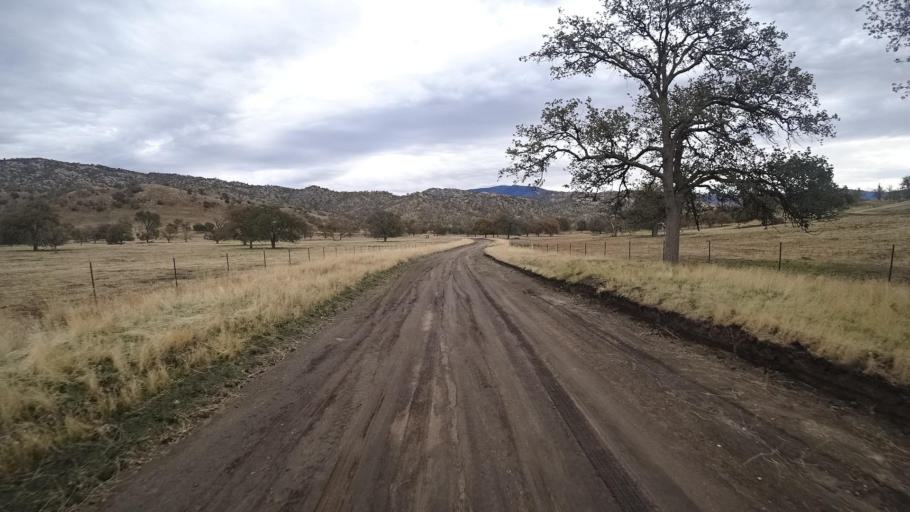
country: US
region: California
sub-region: Kern County
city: Stallion Springs
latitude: 35.1220
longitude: -118.7052
